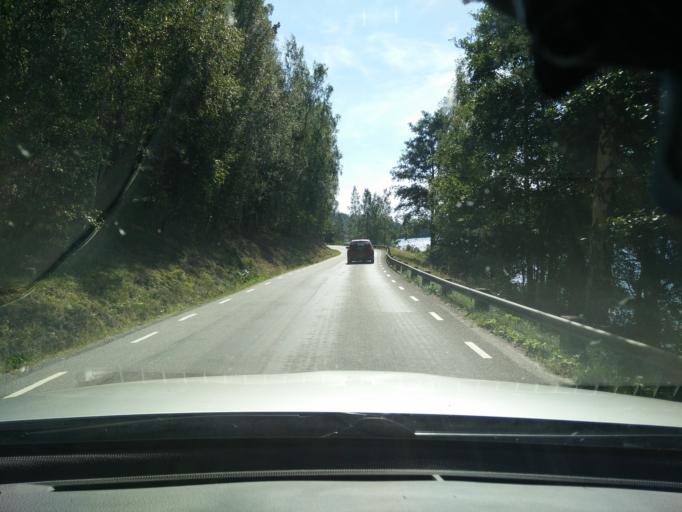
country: SE
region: OEstergoetland
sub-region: Norrkopings Kommun
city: Jursla
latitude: 58.7032
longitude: 16.1544
